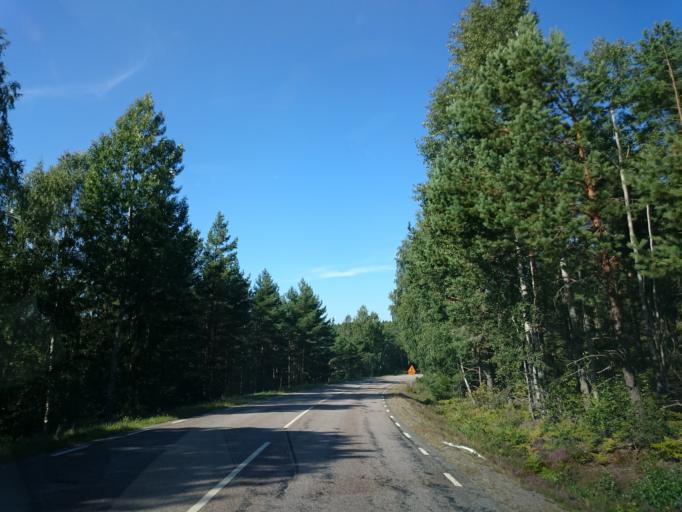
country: SE
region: OEstergoetland
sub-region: Norrkopings Kommun
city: Krokek
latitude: 58.6507
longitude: 16.5472
